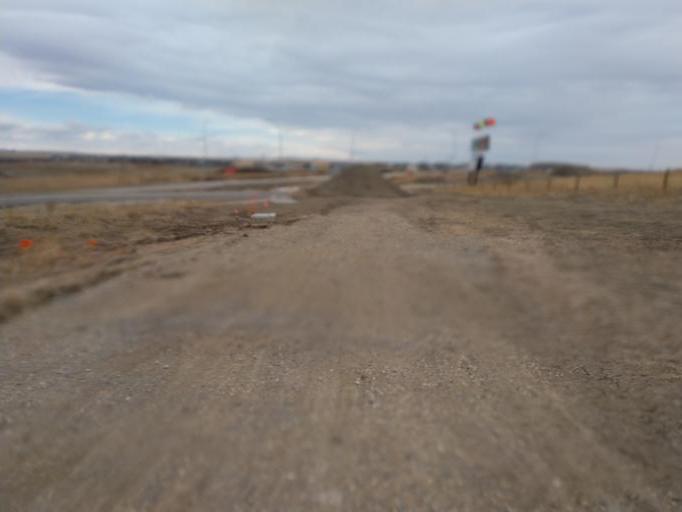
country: CA
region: Alberta
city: Airdrie
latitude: 51.1768
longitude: -114.0688
